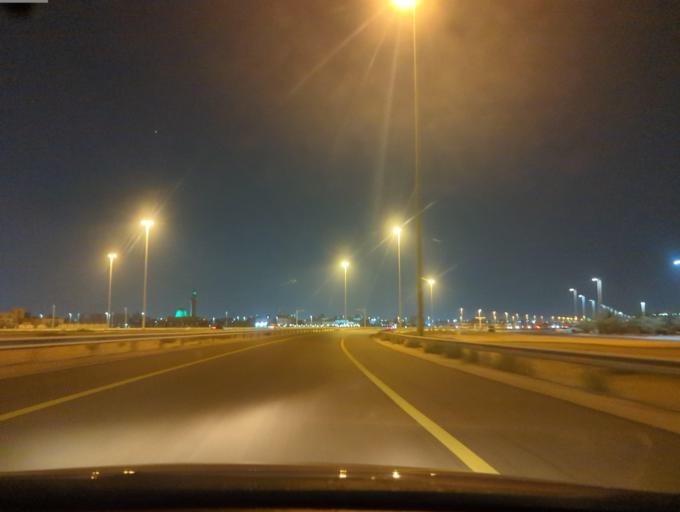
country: AE
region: Abu Dhabi
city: Abu Dhabi
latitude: 24.3802
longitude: 54.7304
